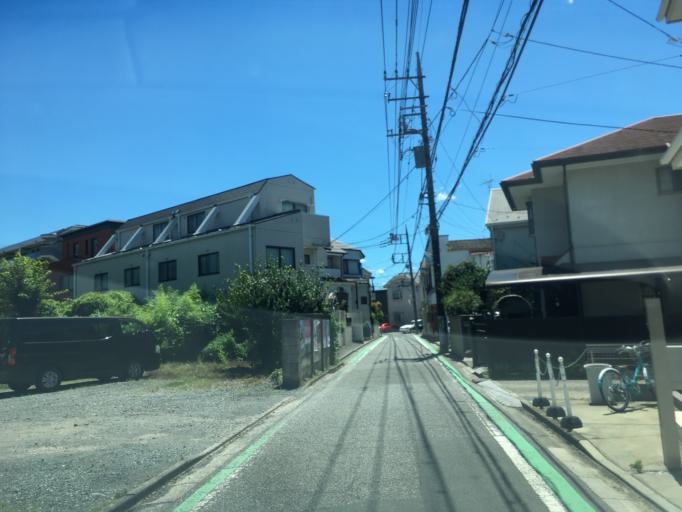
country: JP
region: Tokyo
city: Higashimurayama-shi
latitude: 35.7486
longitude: 139.4605
